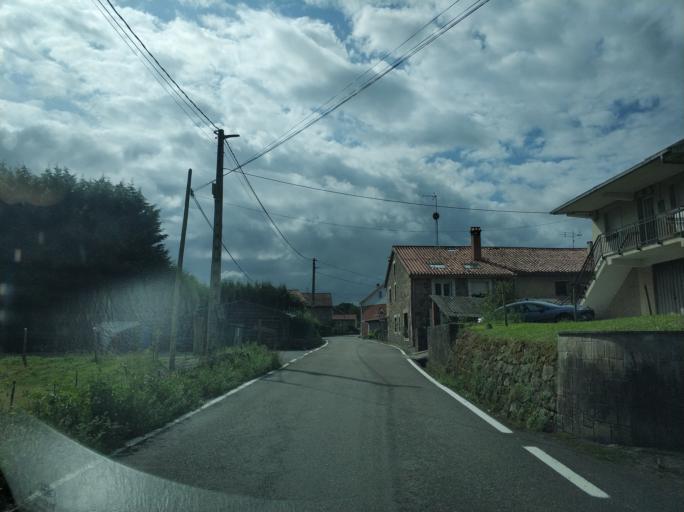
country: ES
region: Cantabria
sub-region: Provincia de Cantabria
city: Polanco
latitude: 43.3715
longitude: -3.9703
